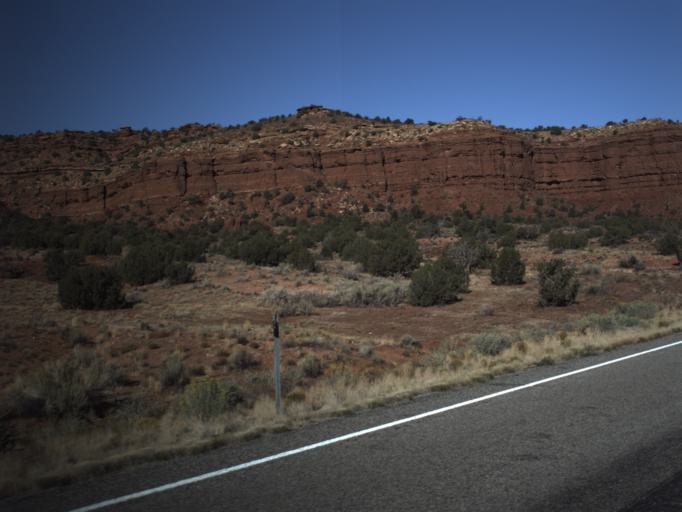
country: US
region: Utah
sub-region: San Juan County
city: Blanding
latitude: 37.6826
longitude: -110.2200
